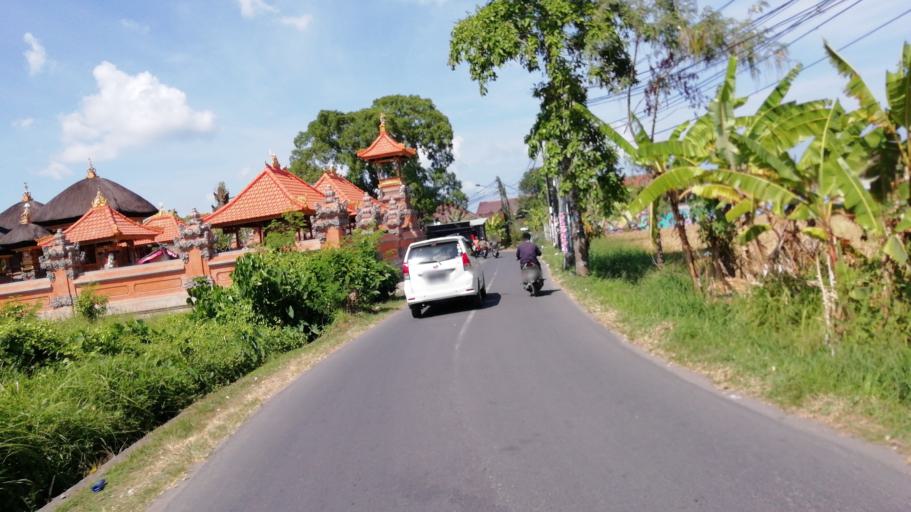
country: ID
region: Bali
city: Banjar Kerobokan
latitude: -8.6525
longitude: 115.1356
